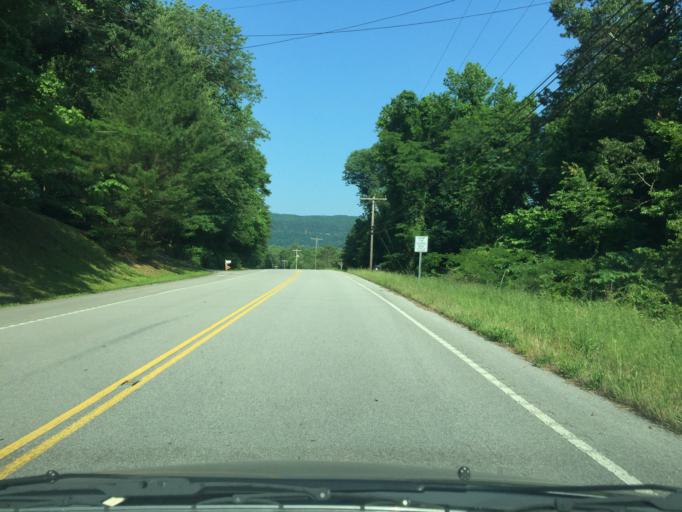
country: US
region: Tennessee
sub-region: Hamilton County
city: Lookout Mountain
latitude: 35.0362
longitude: -85.4137
